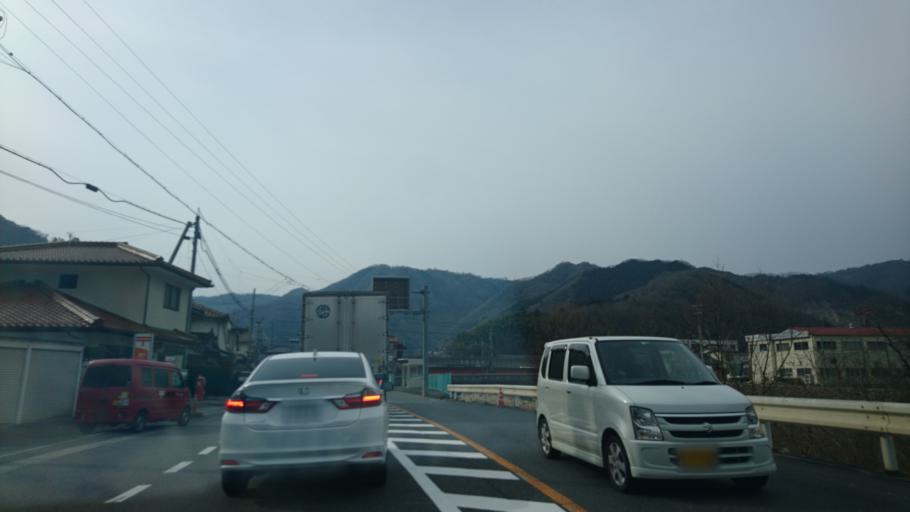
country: JP
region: Okayama
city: Takahashi
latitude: 34.8252
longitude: 133.6198
